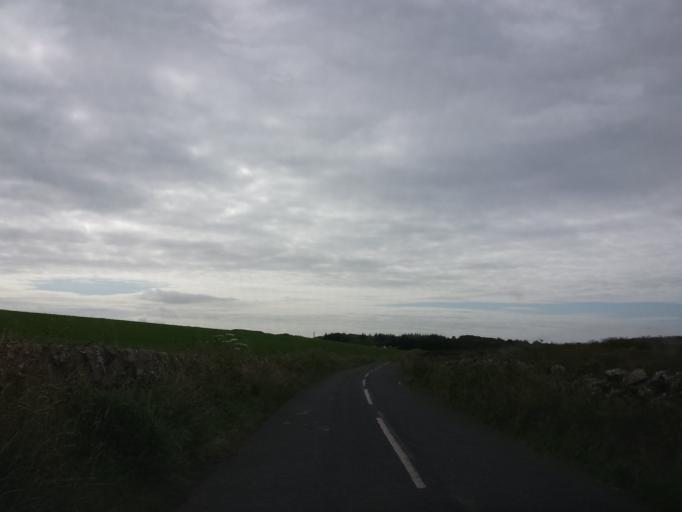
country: GB
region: Scotland
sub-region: Dumfries and Galloway
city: Stranraer
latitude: 54.8748
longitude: -5.1212
